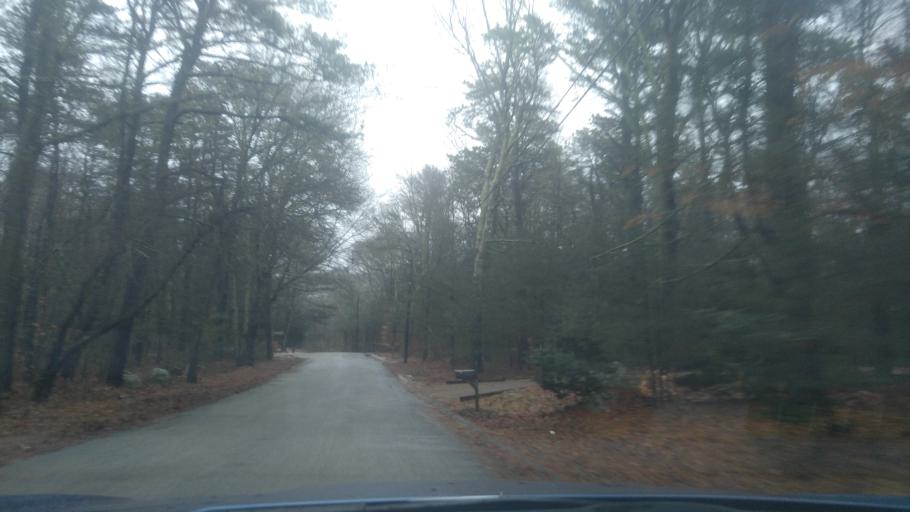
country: US
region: Rhode Island
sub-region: Washington County
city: Charlestown
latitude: 41.4383
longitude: -71.6077
